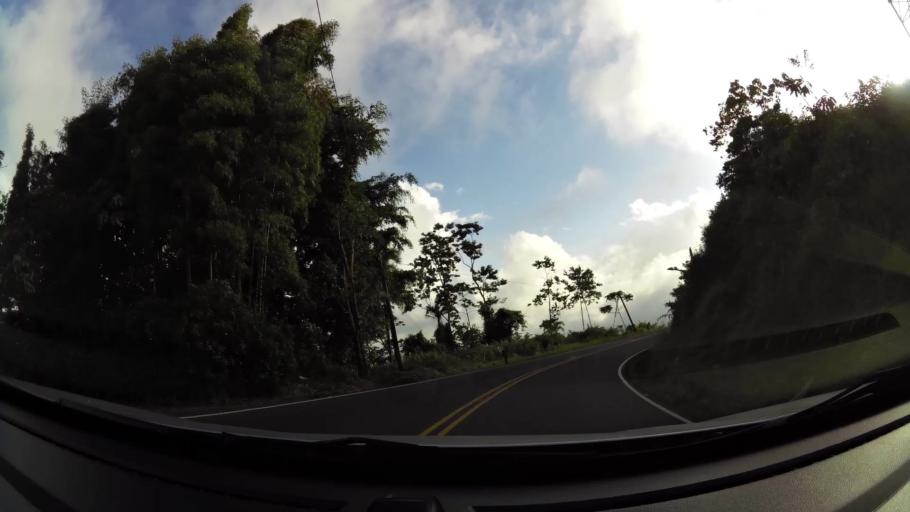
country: CR
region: Limon
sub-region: Canton de Siquirres
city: Siquirres
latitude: 10.0398
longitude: -83.5454
